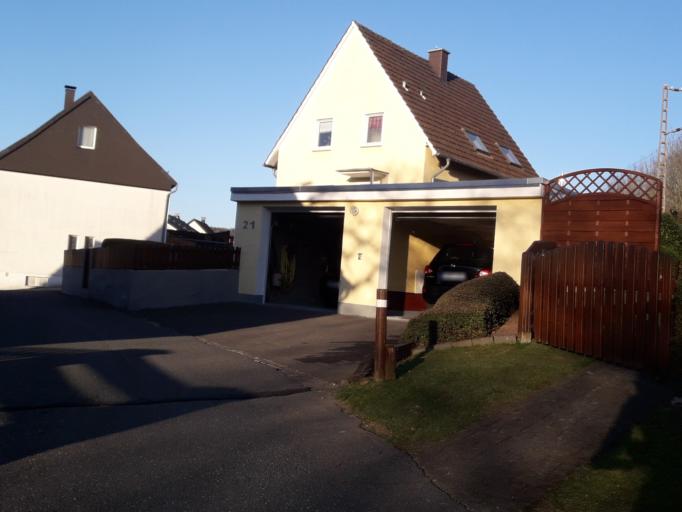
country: DE
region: North Rhine-Westphalia
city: Bad Lippspringe
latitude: 51.7455
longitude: 8.8595
